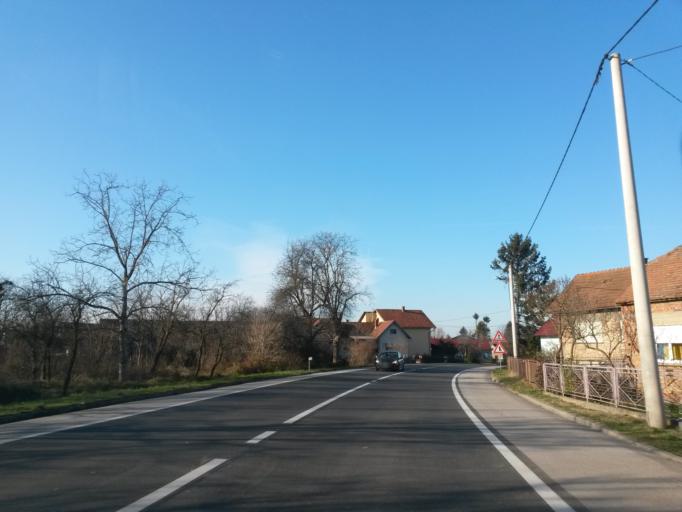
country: HR
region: Varazdinska
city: Jalzabet
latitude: 46.2653
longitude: 16.5182
